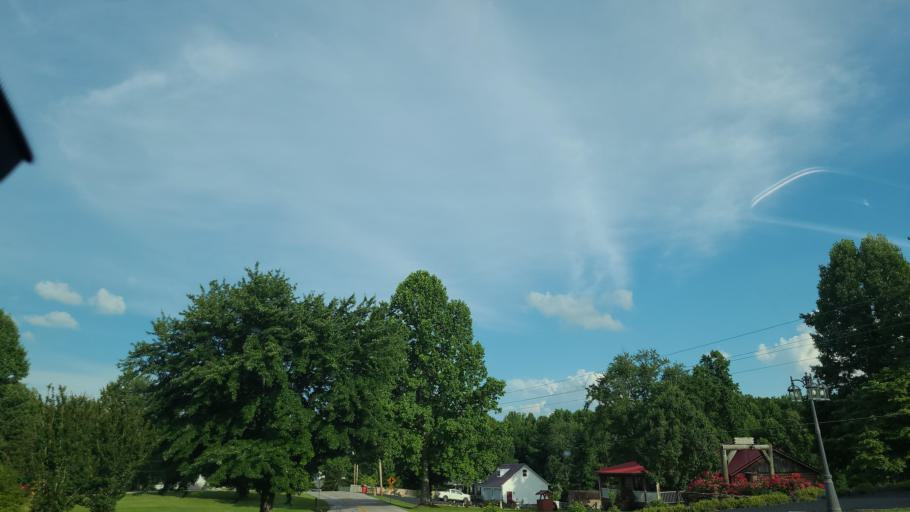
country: US
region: Kentucky
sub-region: Whitley County
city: Corbin
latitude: 36.8965
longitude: -84.2327
